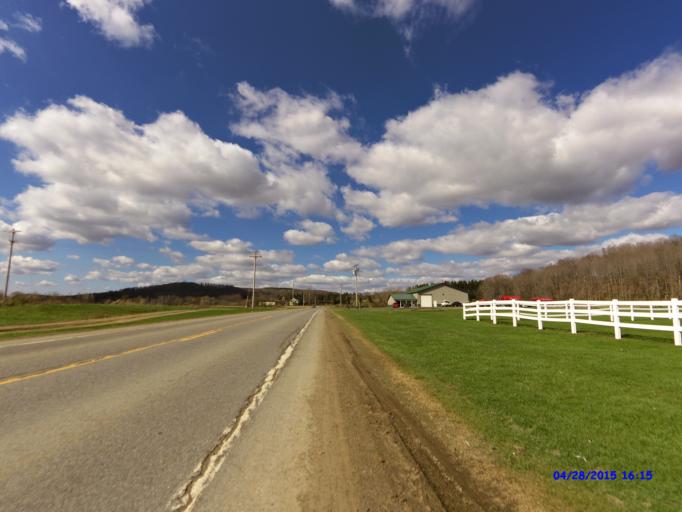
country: US
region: New York
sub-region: Cattaraugus County
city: Franklinville
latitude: 42.3669
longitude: -78.4513
